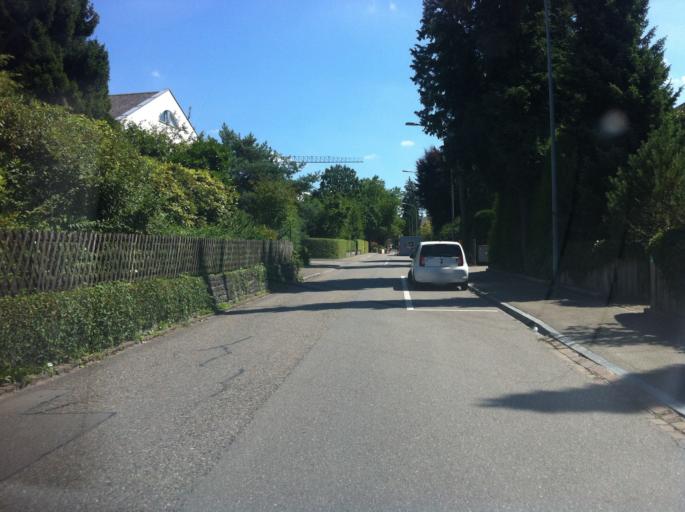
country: CH
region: Zurich
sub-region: Bezirk Zuerich
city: Zuerich (Kreis 8) / Weinegg
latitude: 47.3473
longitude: 8.5668
